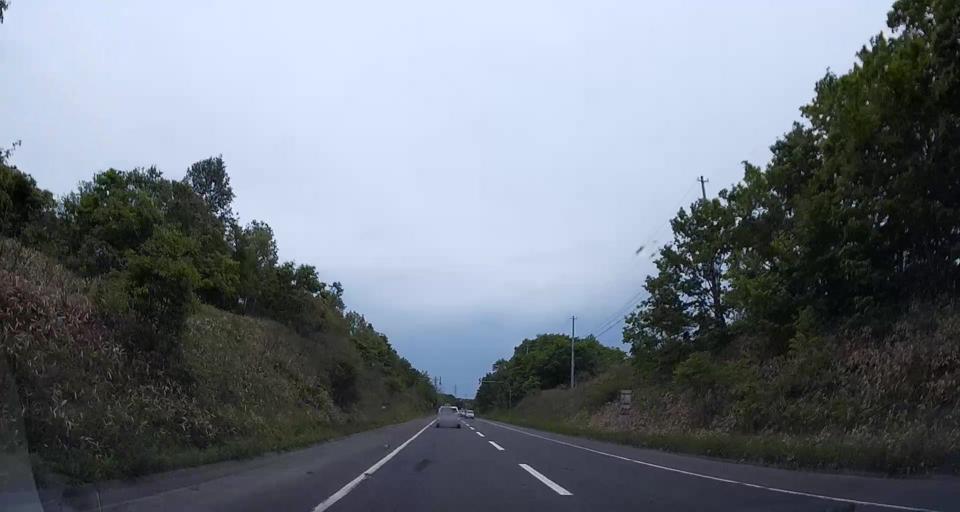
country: JP
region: Hokkaido
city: Chitose
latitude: 42.7023
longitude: 141.7427
